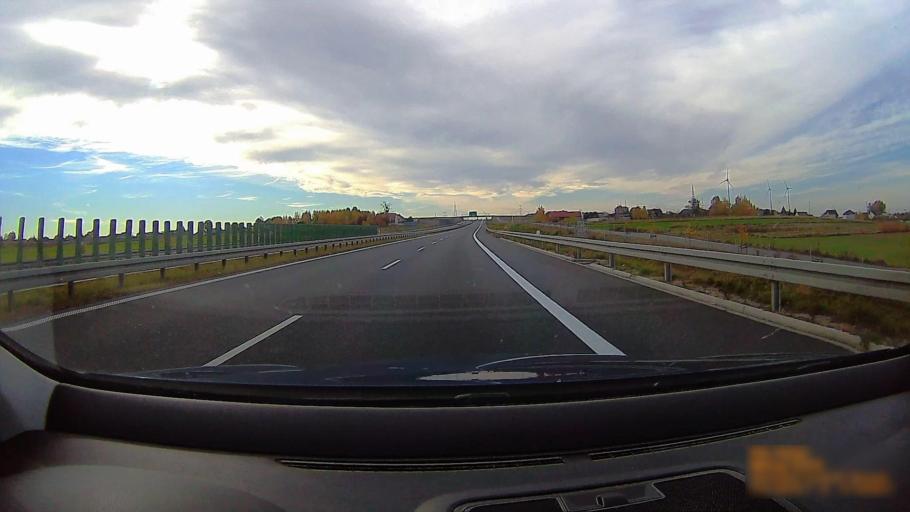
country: PL
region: Greater Poland Voivodeship
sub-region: Powiat ostrowski
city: Przygodzice
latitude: 51.6381
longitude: 17.8745
